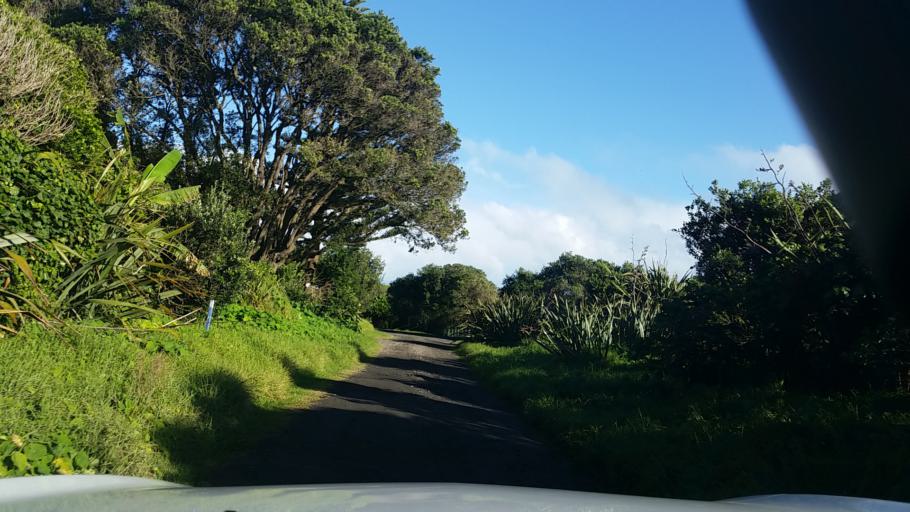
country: NZ
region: Taranaki
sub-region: New Plymouth District
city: New Plymouth
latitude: -39.1194
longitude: 173.9256
